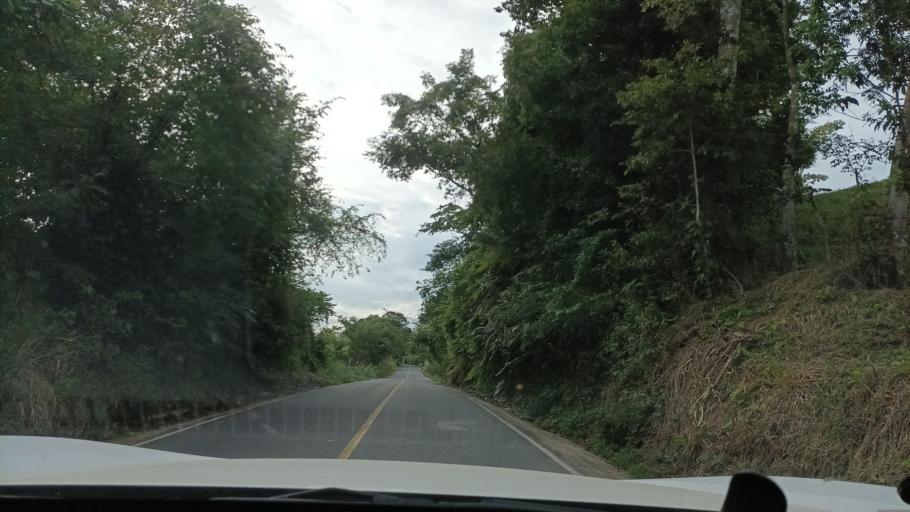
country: MX
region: Veracruz
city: Hidalgotitlan
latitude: 17.7534
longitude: -94.4982
